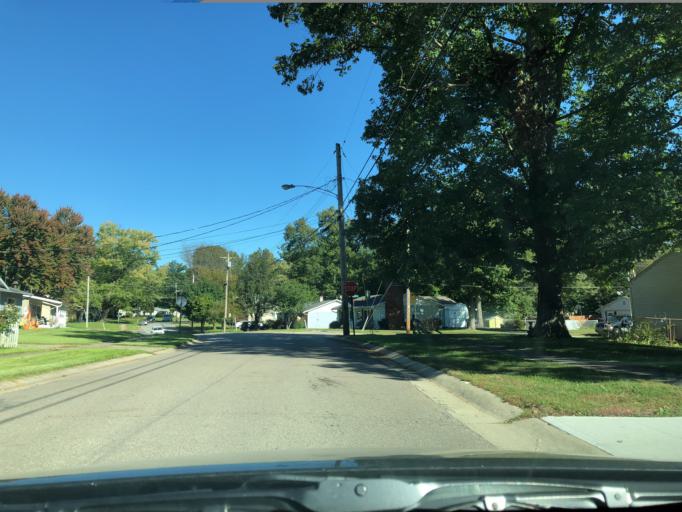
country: US
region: Ohio
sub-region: Hamilton County
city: Loveland
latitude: 39.2633
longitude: -84.2784
